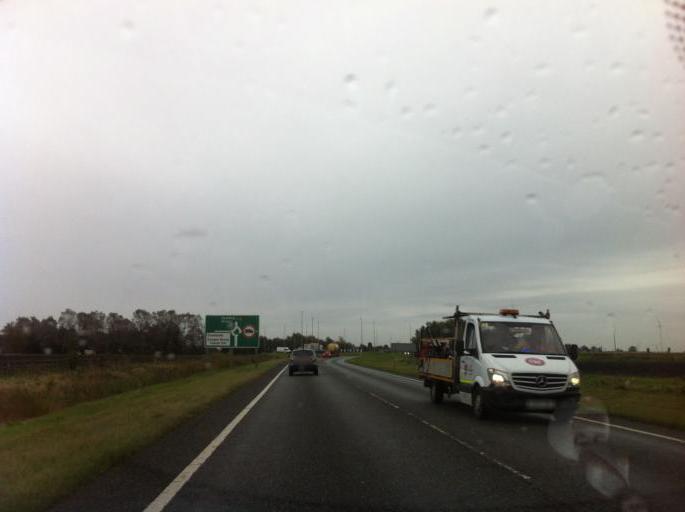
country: GB
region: England
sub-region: Lincolnshire
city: Crowland
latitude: 52.6621
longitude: -0.1743
